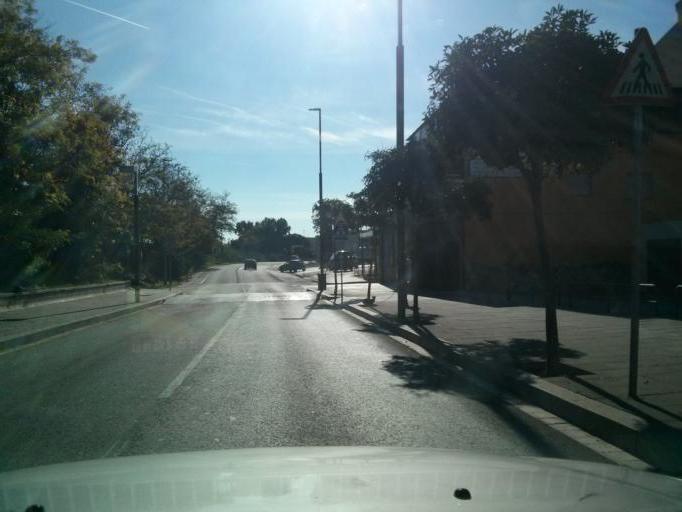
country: ES
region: Catalonia
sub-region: Provincia de Tarragona
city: El Vendrell
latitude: 41.2164
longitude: 1.5357
